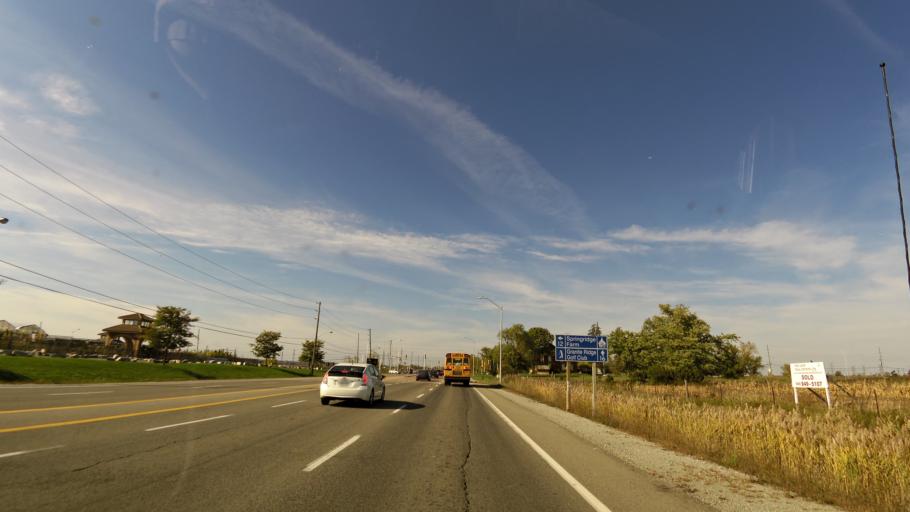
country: CA
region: Ontario
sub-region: Halton
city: Milton
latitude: 43.5541
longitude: -79.8064
